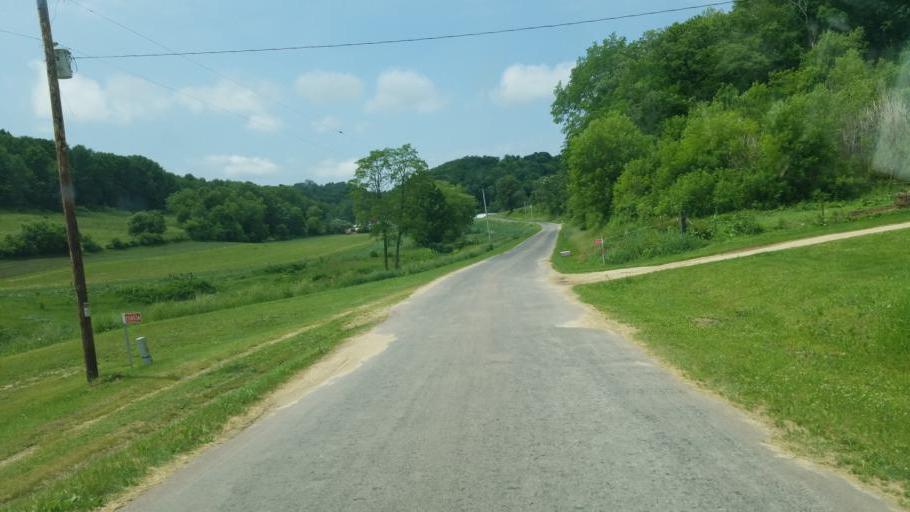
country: US
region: Wisconsin
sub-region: Monroe County
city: Cashton
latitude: 43.7174
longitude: -90.6854
